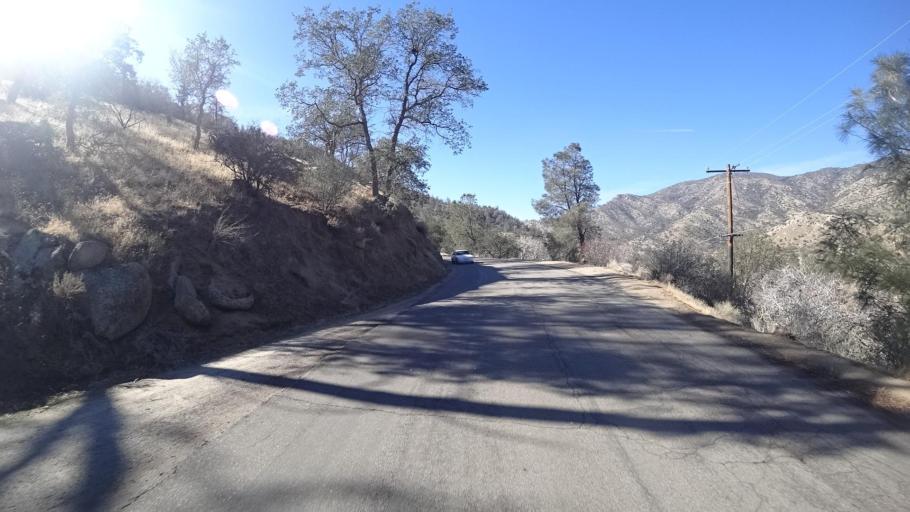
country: US
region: California
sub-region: Kern County
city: Bodfish
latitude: 35.5753
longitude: -118.5440
